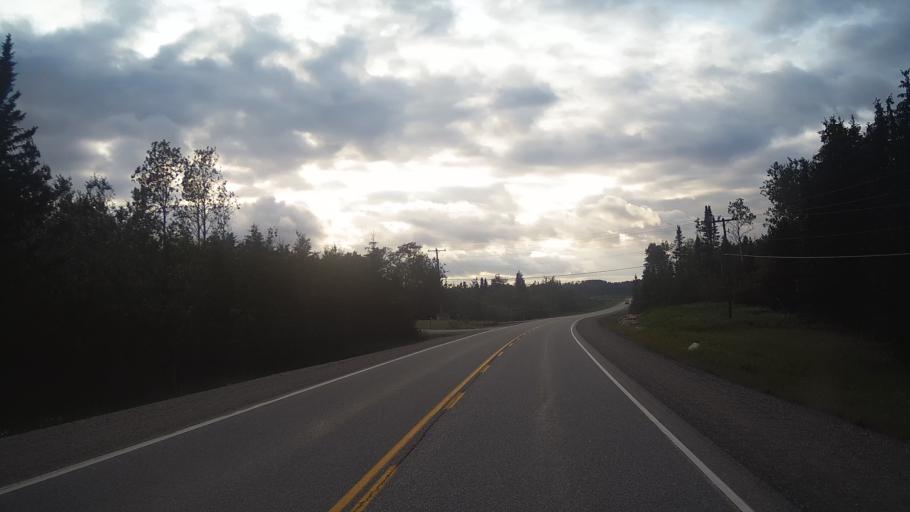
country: CA
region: Ontario
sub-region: Rainy River District
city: Atikokan
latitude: 49.0248
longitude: -90.4507
